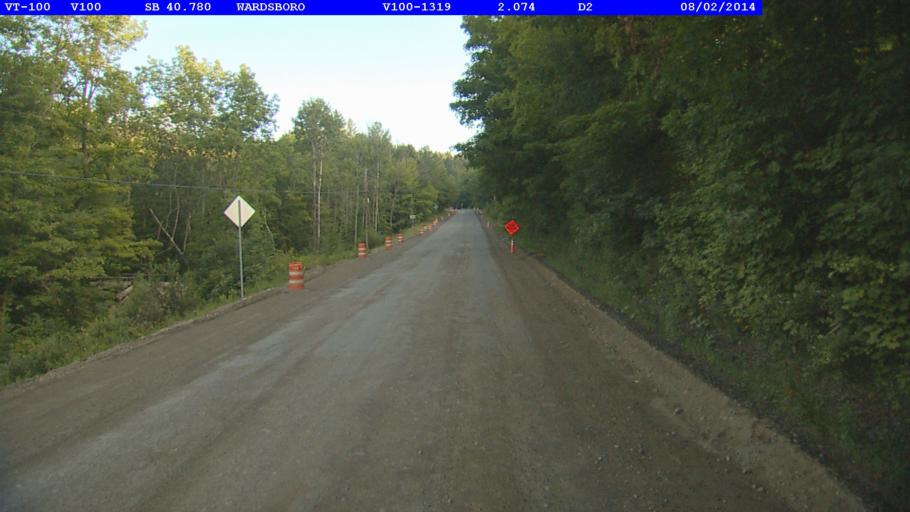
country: US
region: Vermont
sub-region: Windham County
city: Dover
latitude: 43.0271
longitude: -72.8529
